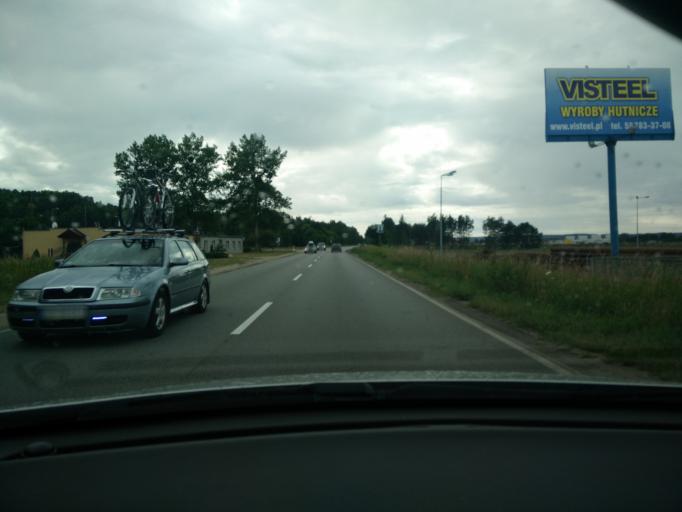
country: PL
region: Pomeranian Voivodeship
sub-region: Powiat pucki
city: Kosakowo
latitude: 54.6046
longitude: 18.4664
